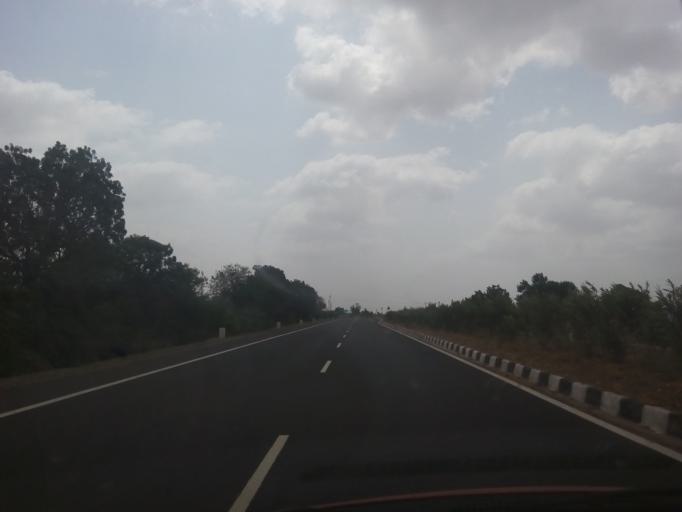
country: IN
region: Gujarat
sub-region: Surendranagar
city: Dhrangadhra
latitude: 23.0006
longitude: 71.5141
